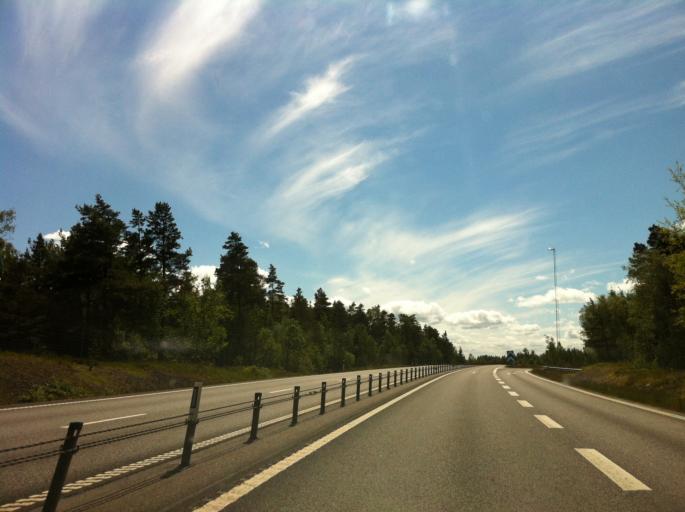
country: SE
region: Vaestra Goetaland
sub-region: Vanersborgs Kommun
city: Vanersborg
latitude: 58.3972
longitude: 12.2971
